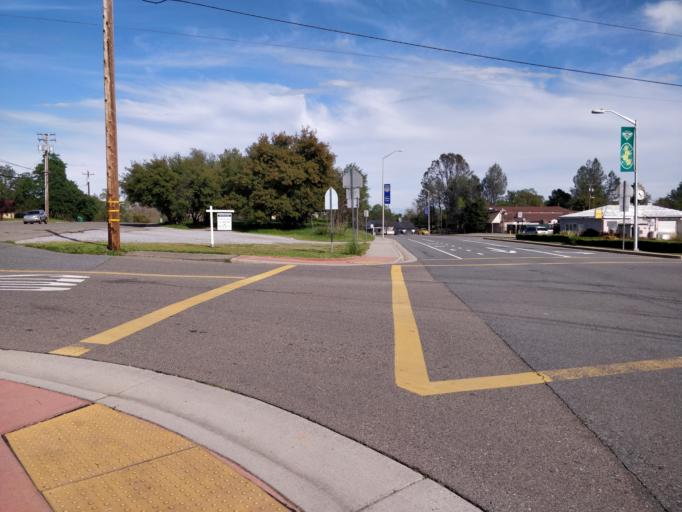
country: US
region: California
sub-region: Shasta County
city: Shasta Lake
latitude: 40.6809
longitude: -122.3673
